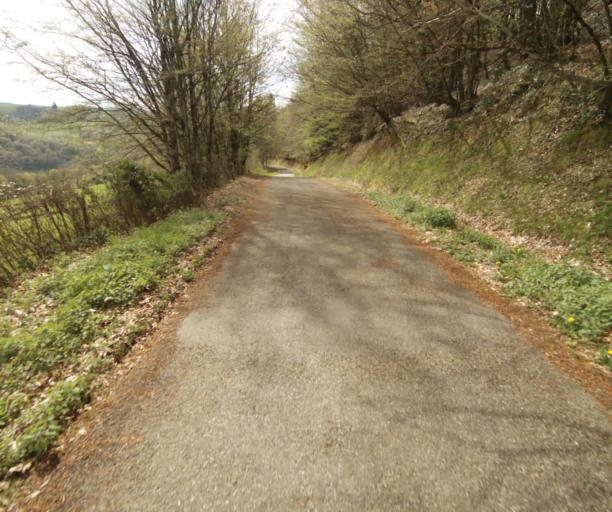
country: FR
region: Limousin
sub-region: Departement de la Correze
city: Laguenne
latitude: 45.2567
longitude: 1.8165
